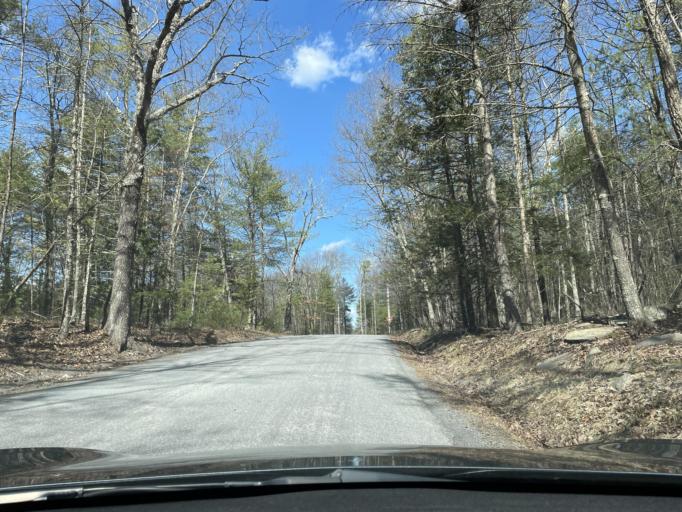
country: US
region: New York
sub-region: Ulster County
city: West Hurley
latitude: 41.9628
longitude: -74.1113
